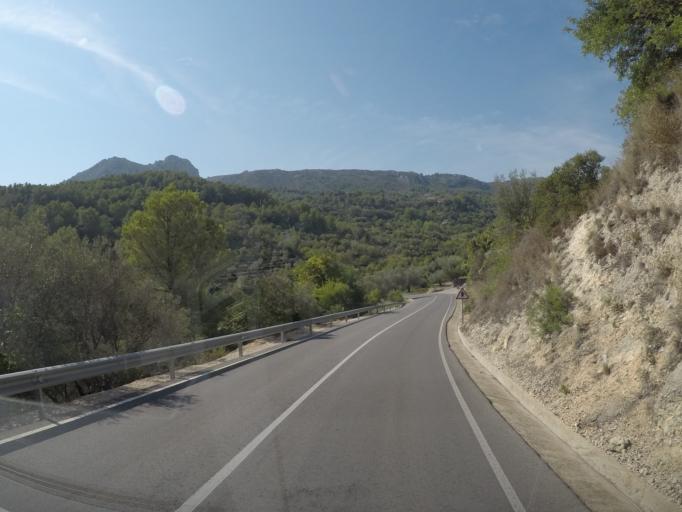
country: ES
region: Valencia
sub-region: Provincia de Alicante
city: Murla
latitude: 38.7803
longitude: -0.0982
